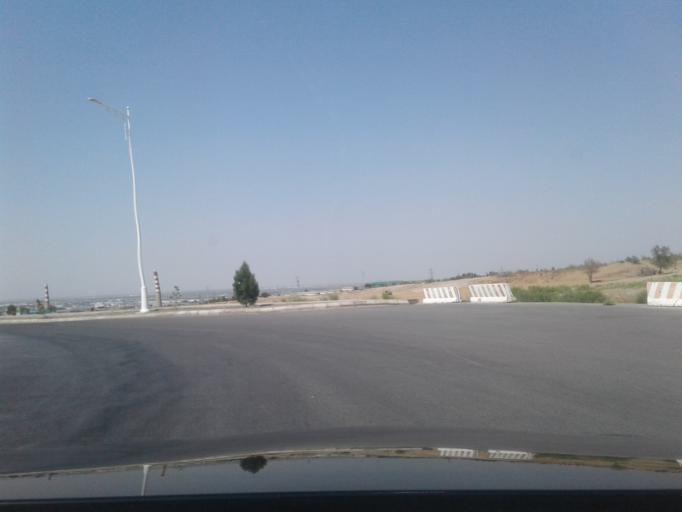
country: TM
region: Ahal
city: Ashgabat
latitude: 37.8950
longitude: 58.4234
